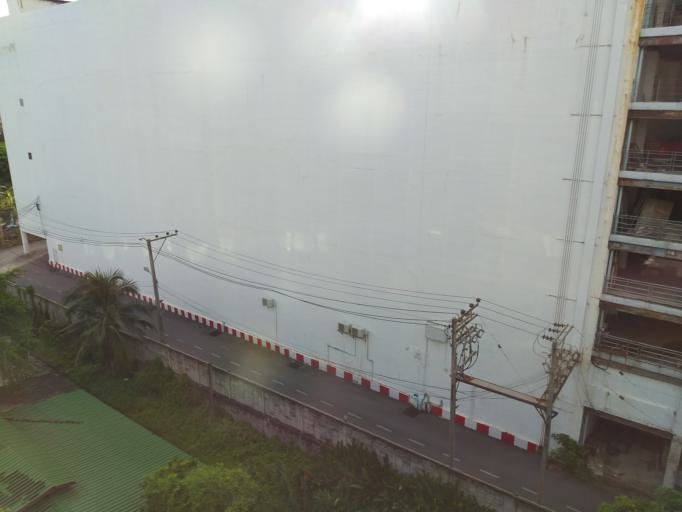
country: TH
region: Nonthaburi
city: Mueang Nonthaburi
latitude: 13.8580
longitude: 100.5176
